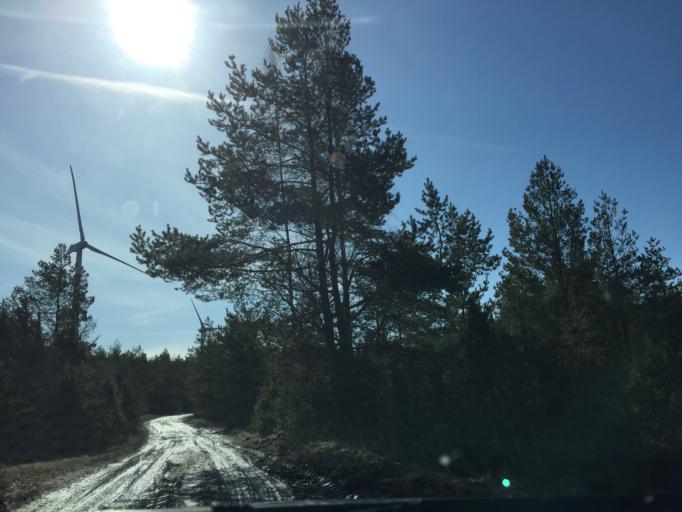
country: EE
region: Laeaene
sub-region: Haapsalu linn
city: Haapsalu
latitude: 58.6422
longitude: 23.5162
